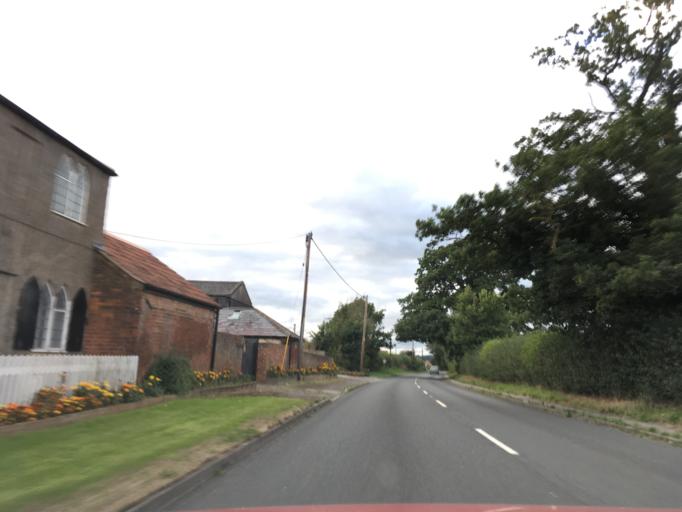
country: GB
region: England
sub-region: Wiltshire
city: Devizes
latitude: 51.3580
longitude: -2.0126
